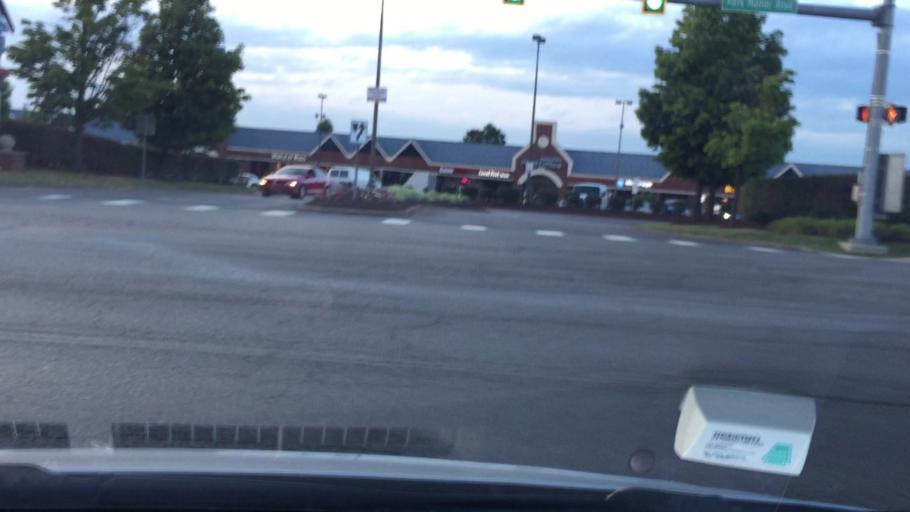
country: US
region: Pennsylvania
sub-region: Allegheny County
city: Oakdale
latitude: 40.4534
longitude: -80.1679
